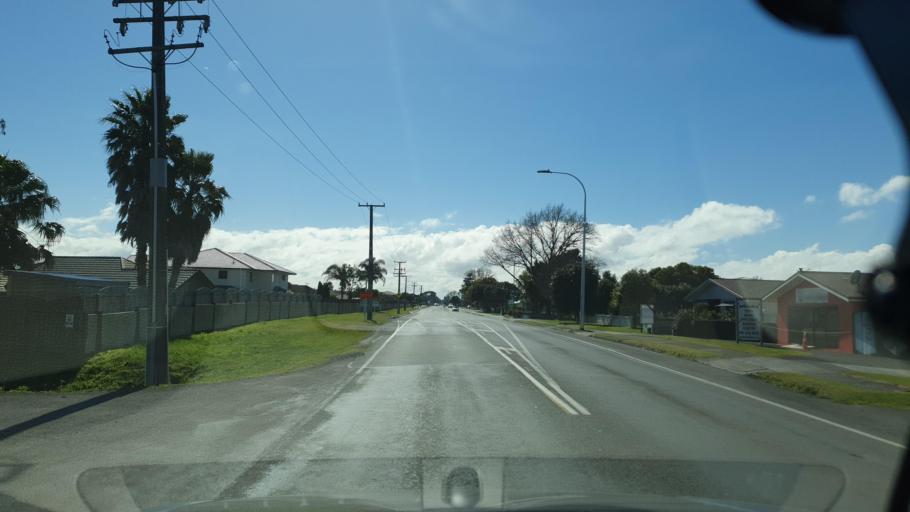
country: NZ
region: Bay of Plenty
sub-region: Tauranga City
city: Tauranga
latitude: -37.7092
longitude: 176.2847
